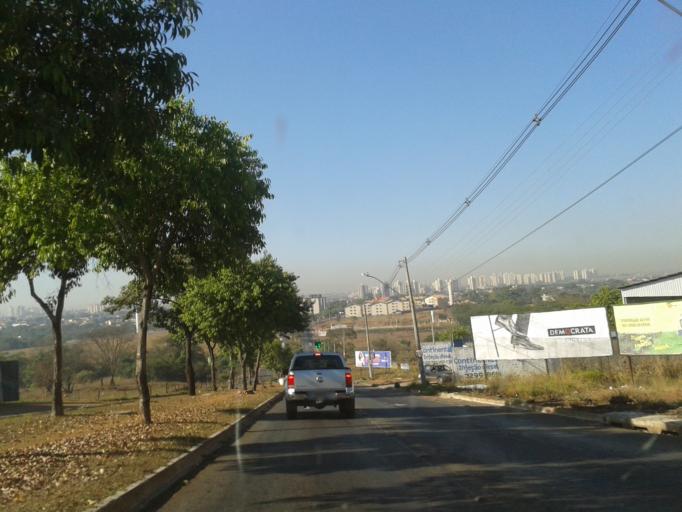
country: BR
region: Goias
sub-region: Goiania
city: Goiania
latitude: -16.6716
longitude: -49.3309
